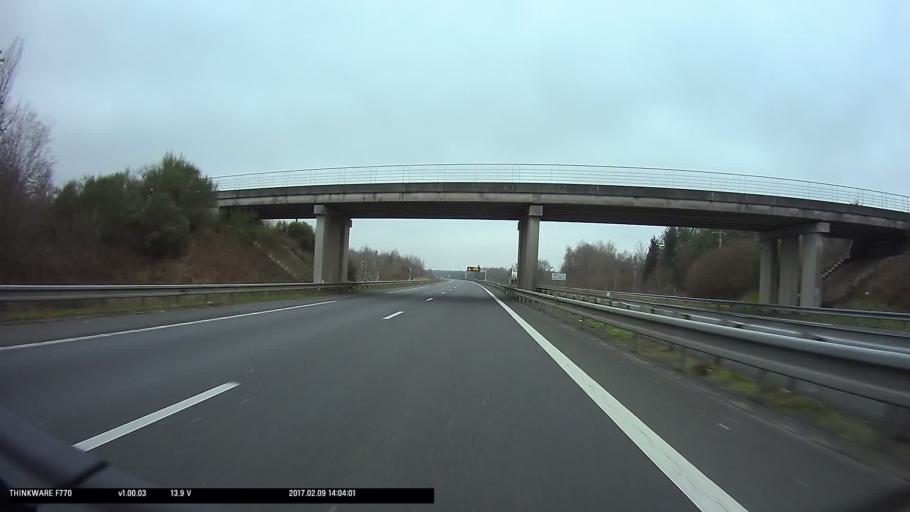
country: FR
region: Centre
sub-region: Departement du Loir-et-Cher
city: Nouan-le-Fuzelier
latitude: 47.5509
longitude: 2.0089
